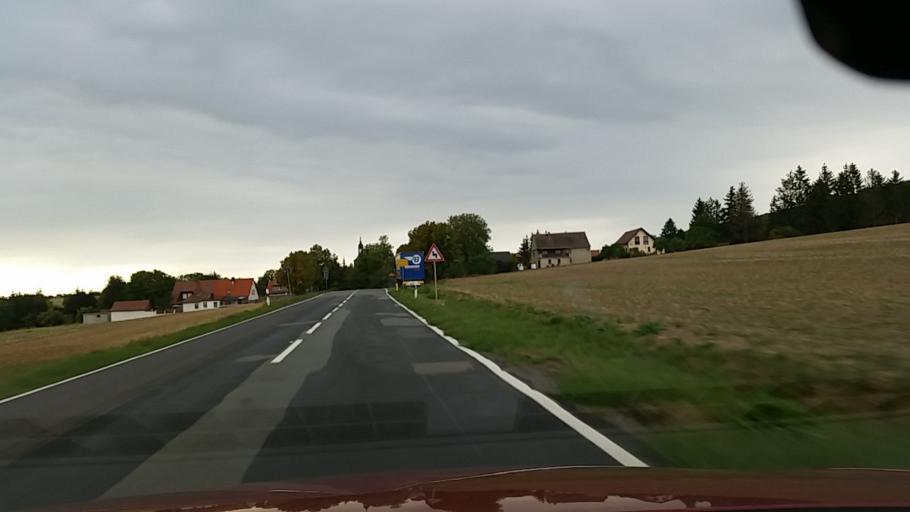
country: DE
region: Saxony-Anhalt
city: Eckartsberga
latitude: 51.1256
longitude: 11.5342
